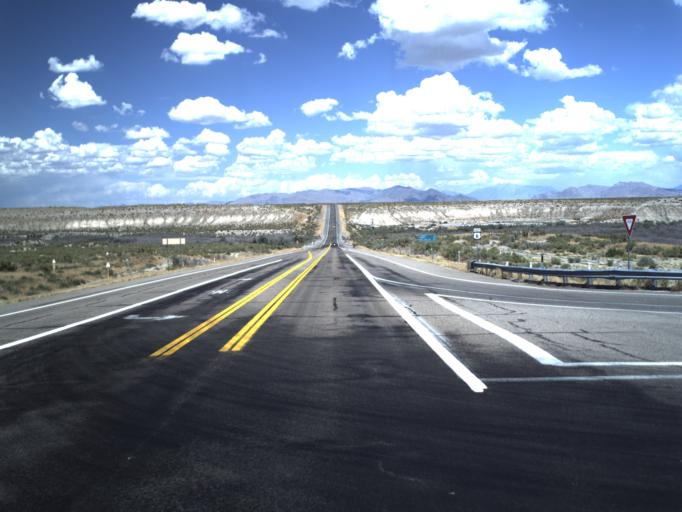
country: US
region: Utah
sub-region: Millard County
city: Delta
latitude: 39.3964
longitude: -112.5039
